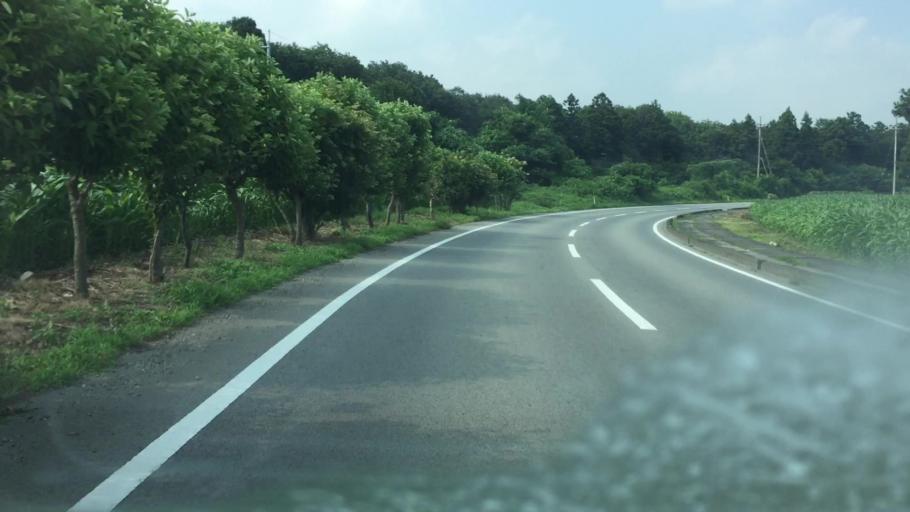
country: JP
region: Tochigi
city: Kuroiso
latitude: 36.9981
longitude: 139.9957
